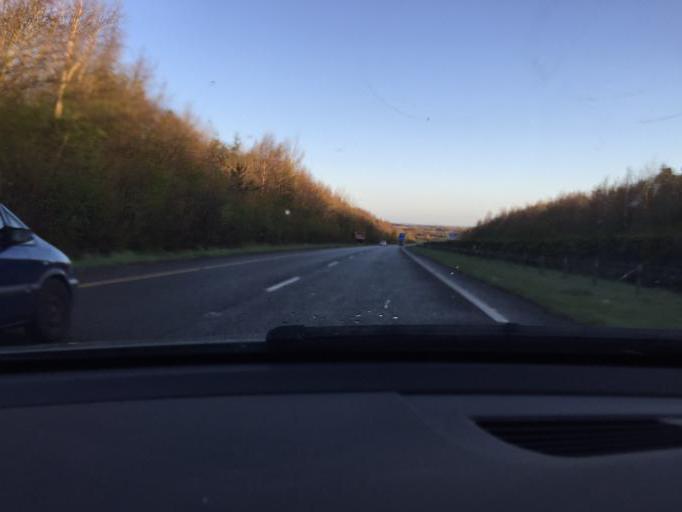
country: IE
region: Leinster
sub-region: An Mhi
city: Stamullin
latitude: 53.6223
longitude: -6.2475
